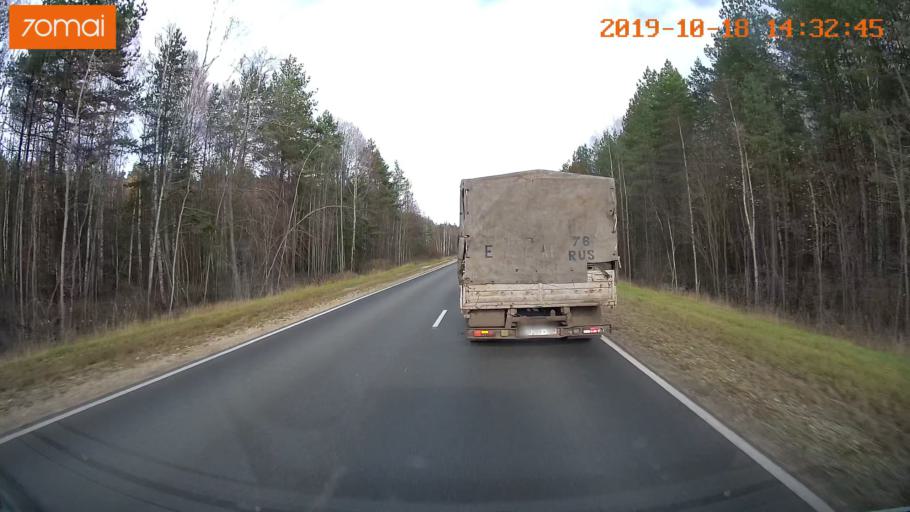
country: RU
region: Rjazan
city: Tuma
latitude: 55.1942
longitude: 40.5847
